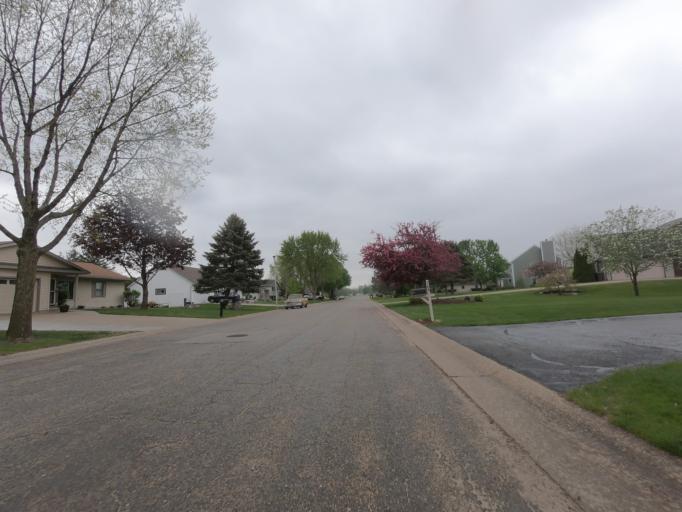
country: US
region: Wisconsin
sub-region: Jefferson County
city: Jefferson
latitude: 43.0148
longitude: -88.8115
